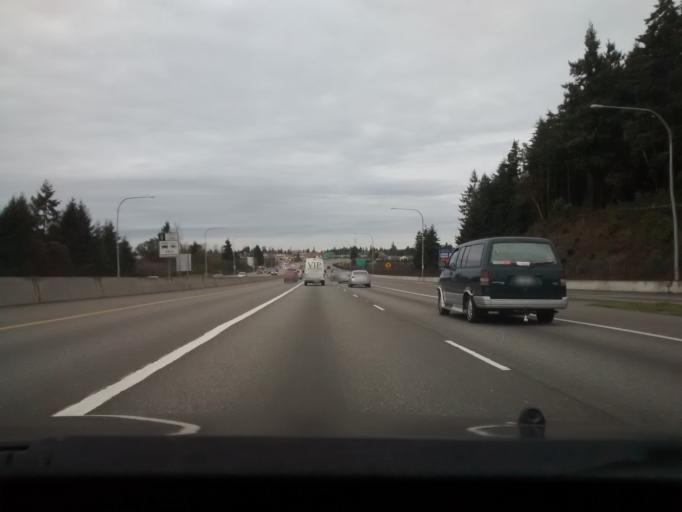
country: US
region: Washington
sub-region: Pierce County
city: Fircrest
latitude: 47.2468
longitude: -122.5080
